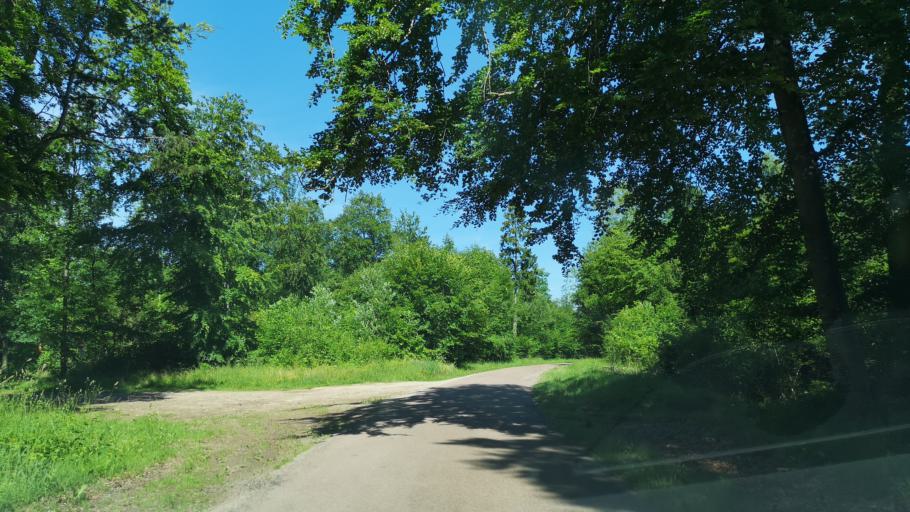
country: FR
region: Lorraine
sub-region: Departement de la Meuse
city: Vigneulles-les-Hattonchatel
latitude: 49.0285
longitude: 5.6432
